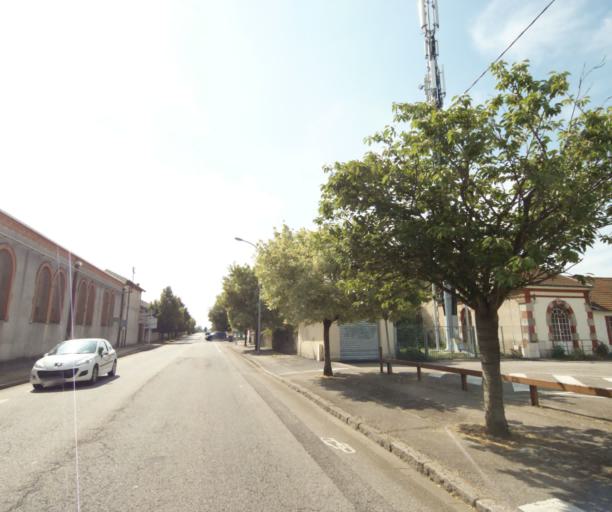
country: FR
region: Lorraine
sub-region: Departement de Meurthe-et-Moselle
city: Chanteheux
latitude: 48.5822
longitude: 6.5168
